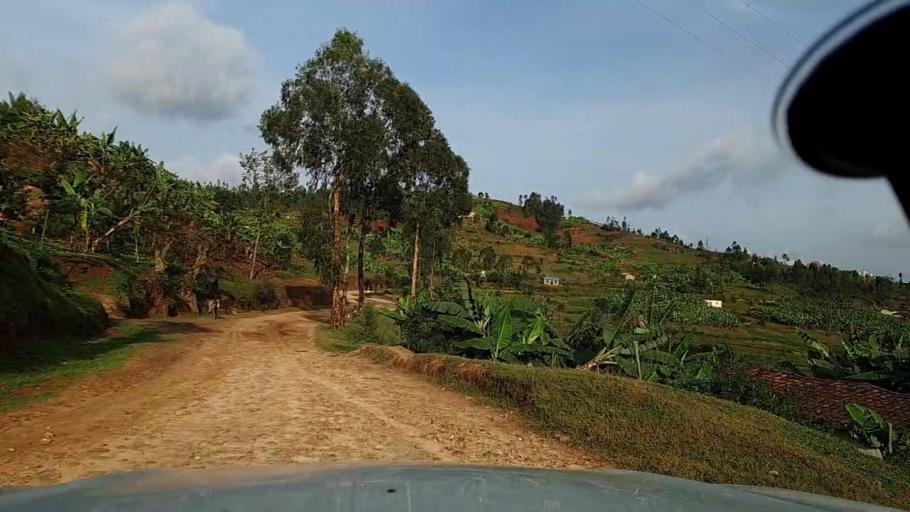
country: RW
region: Southern Province
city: Gitarama
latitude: -2.1822
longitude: 29.5600
